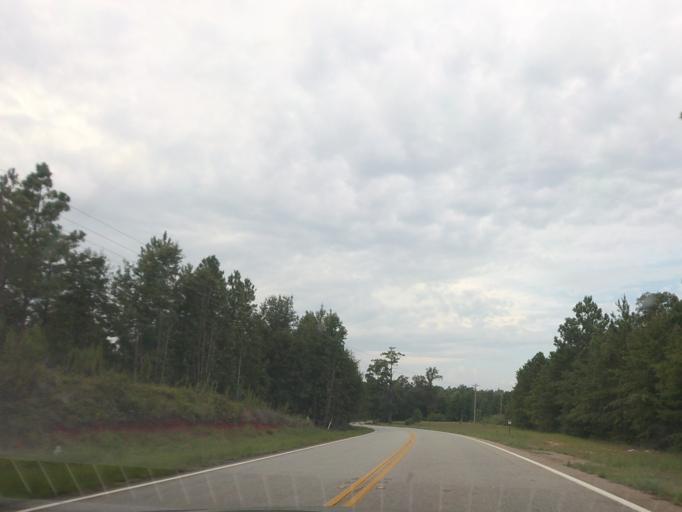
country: US
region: Georgia
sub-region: Twiggs County
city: Jeffersonville
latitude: 32.7434
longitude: -83.4266
